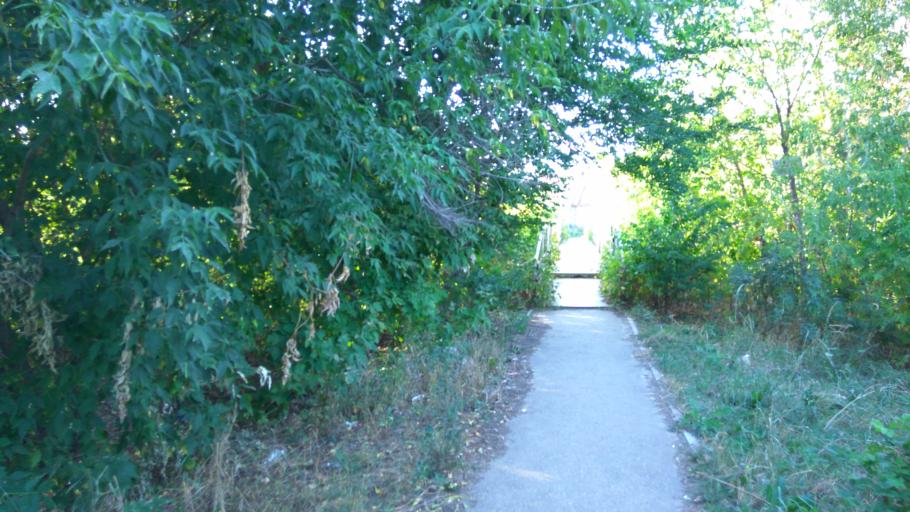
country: RU
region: Tatarstan
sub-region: Gorod Kazan'
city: Kazan
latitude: 55.7360
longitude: 49.0961
